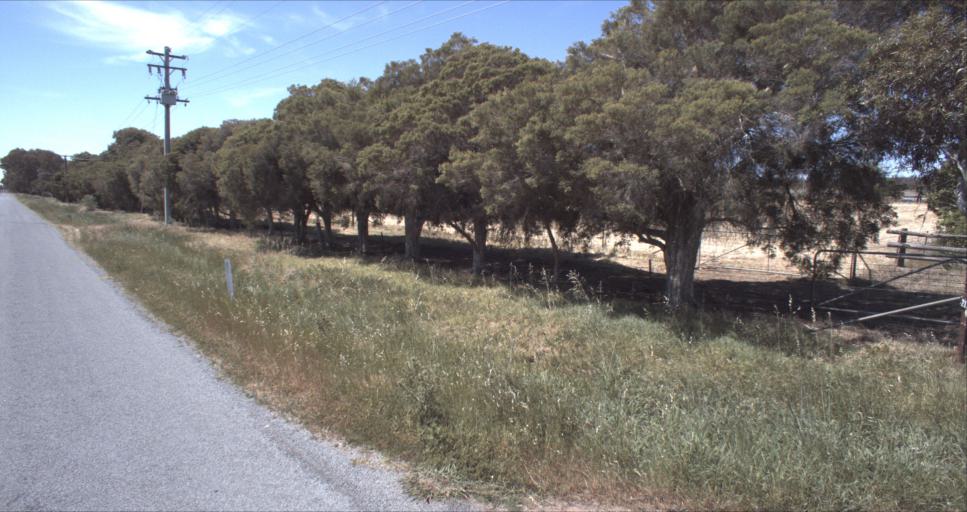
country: AU
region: New South Wales
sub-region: Leeton
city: Leeton
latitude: -34.5835
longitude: 146.4200
